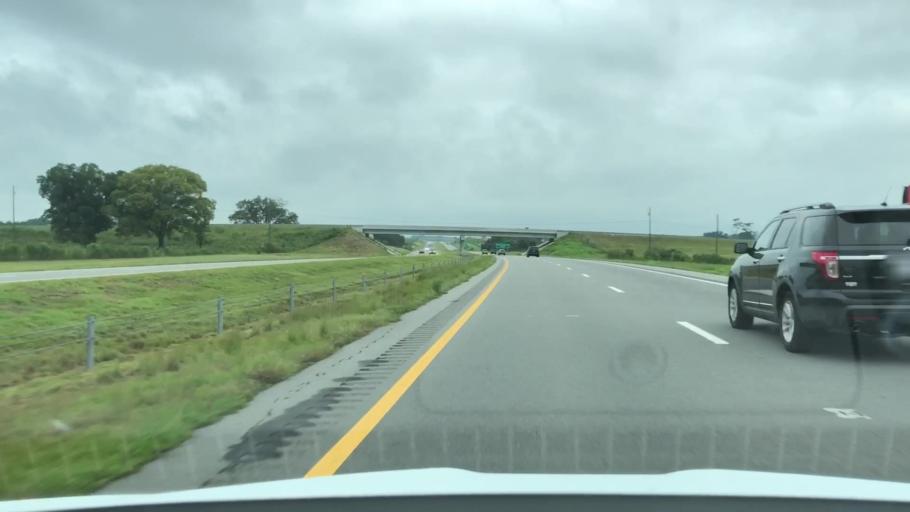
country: US
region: North Carolina
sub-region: Wayne County
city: Elroy
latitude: 35.4025
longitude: -77.8761
